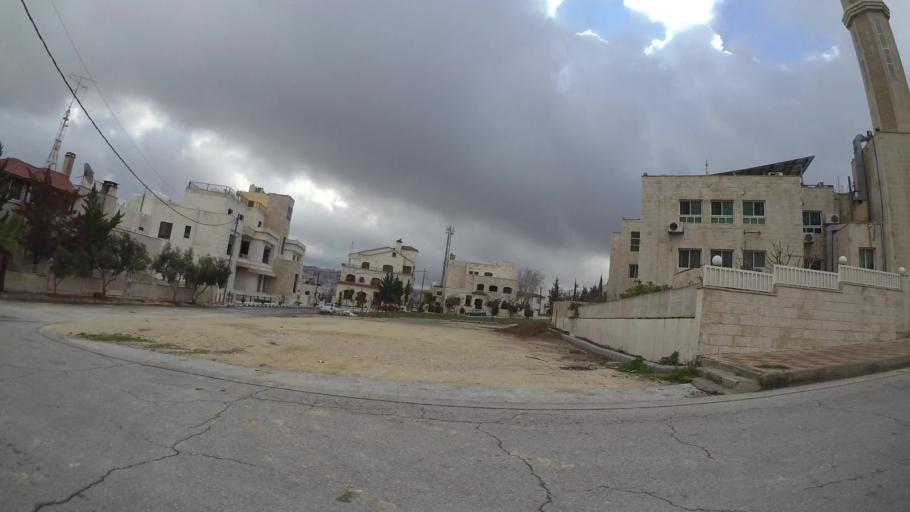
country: JO
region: Amman
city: Amman
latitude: 31.9423
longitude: 35.9040
